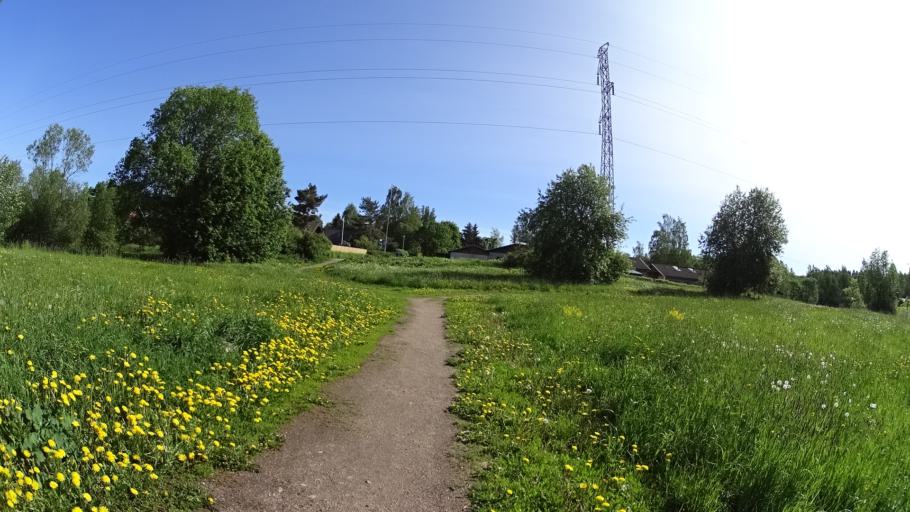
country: FI
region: Uusimaa
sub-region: Helsinki
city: Kilo
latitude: 60.2657
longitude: 24.7913
